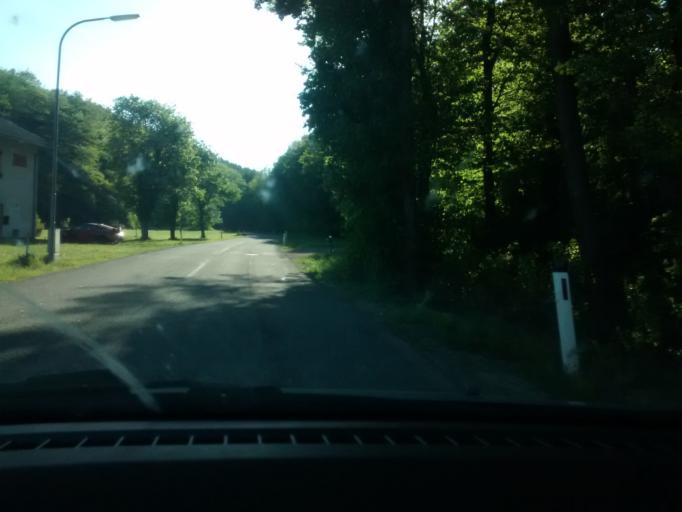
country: AT
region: Lower Austria
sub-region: Politischer Bezirk Baden
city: Klausen-Leopoldsdorf
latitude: 48.0994
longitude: 15.9693
